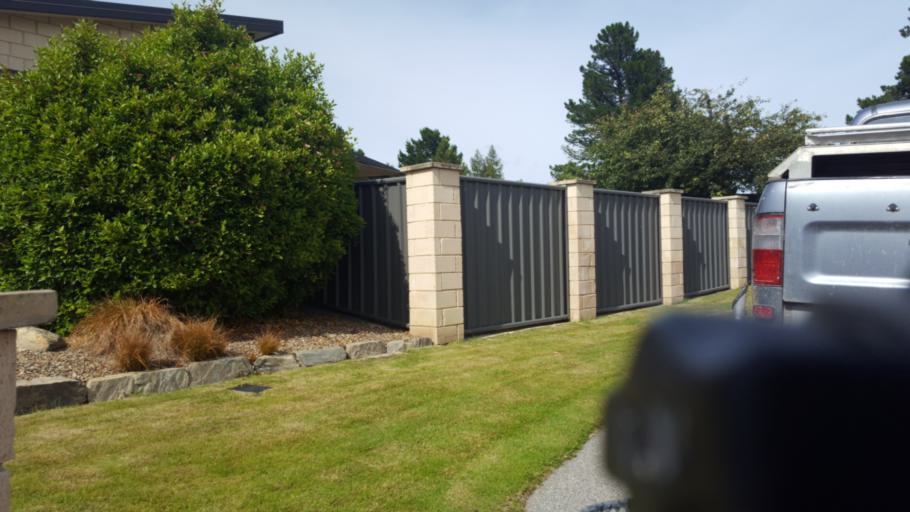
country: NZ
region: Otago
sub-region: Queenstown-Lakes District
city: Wanaka
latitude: -45.0452
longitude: 169.1879
